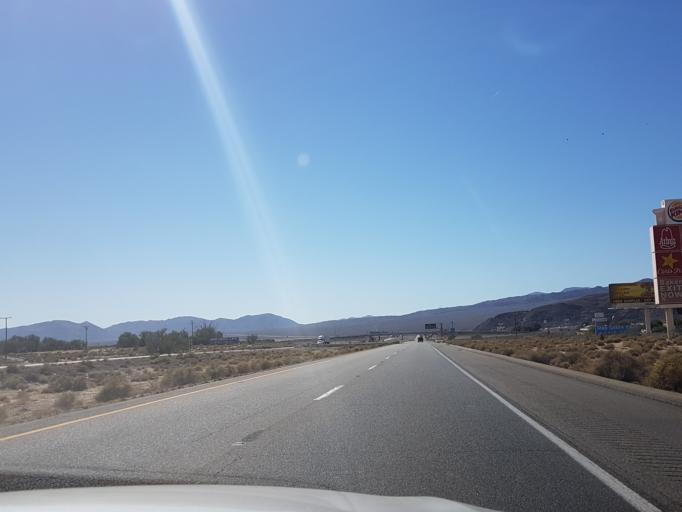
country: US
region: California
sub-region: San Bernardino County
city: Fort Irwin
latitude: 35.2681
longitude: -116.0661
